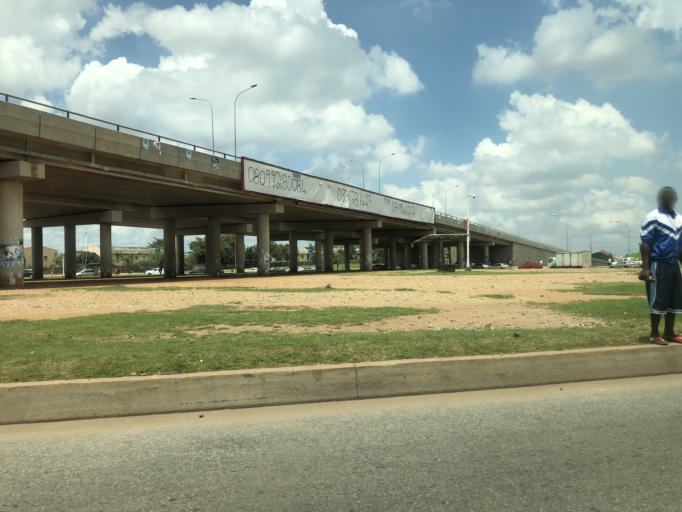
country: NG
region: Abuja Federal Capital Territory
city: Abuja
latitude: 9.0507
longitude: 7.5266
